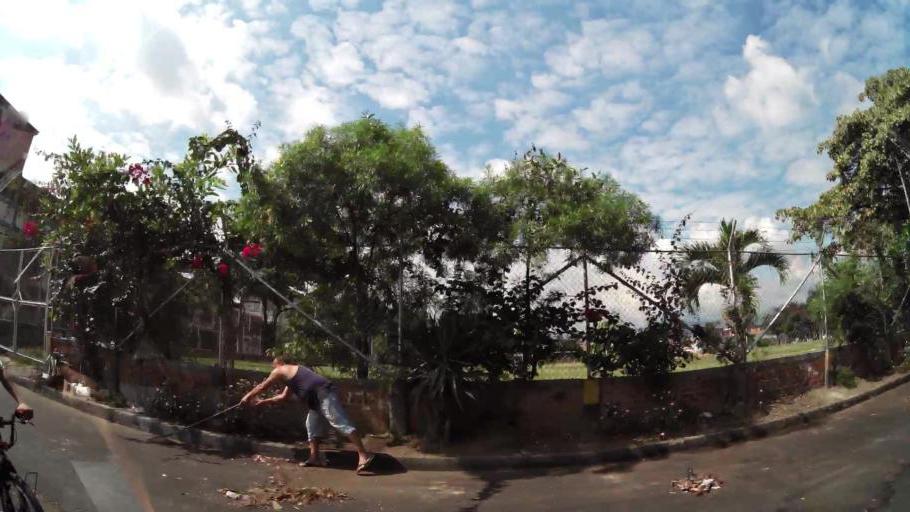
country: CO
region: Valle del Cauca
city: Cali
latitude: 3.4985
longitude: -76.4940
